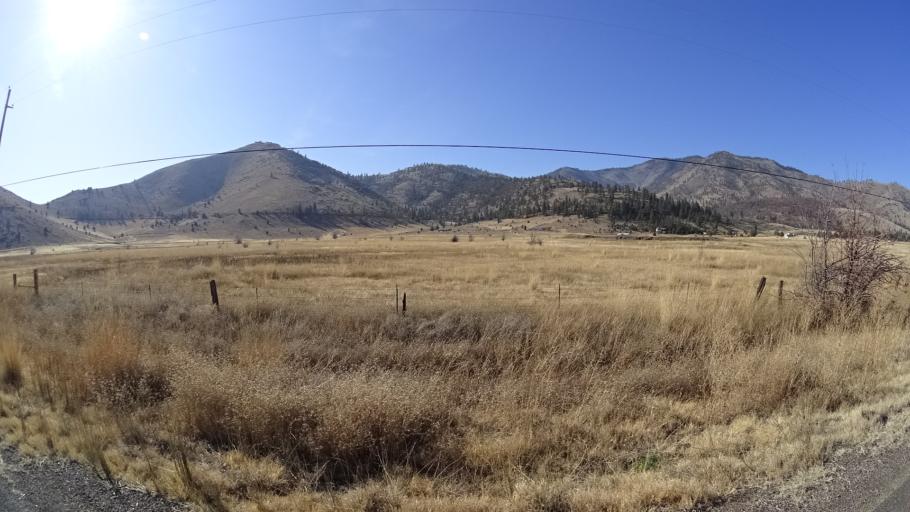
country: US
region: California
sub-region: Siskiyou County
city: Weed
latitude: 41.4723
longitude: -122.4784
